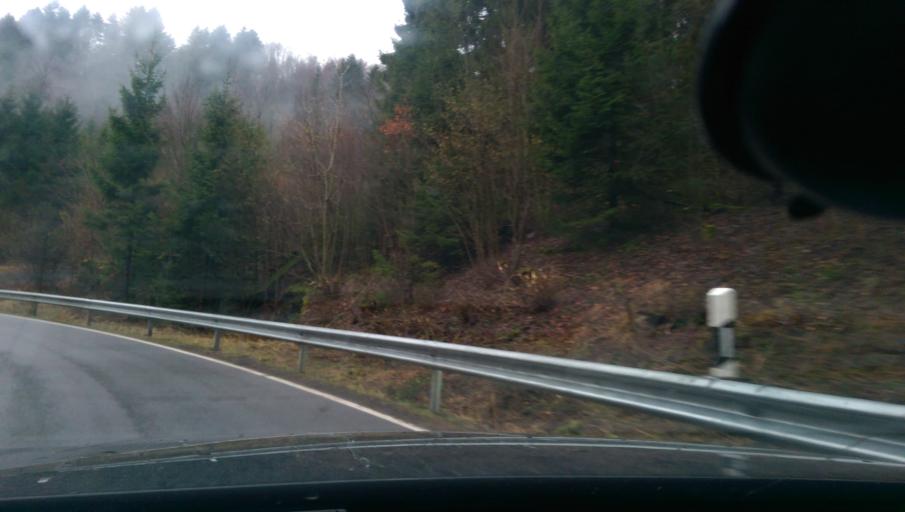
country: DE
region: North Rhine-Westphalia
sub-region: Regierungsbezirk Arnsberg
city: Finnentrop
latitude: 51.2384
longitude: 7.9566
